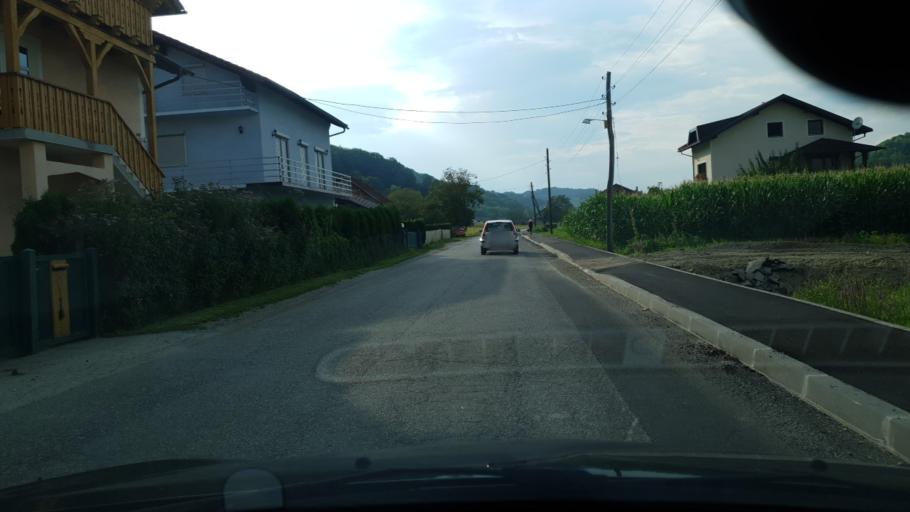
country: HR
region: Krapinsko-Zagorska
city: Zabok
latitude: 46.0795
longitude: 15.8986
